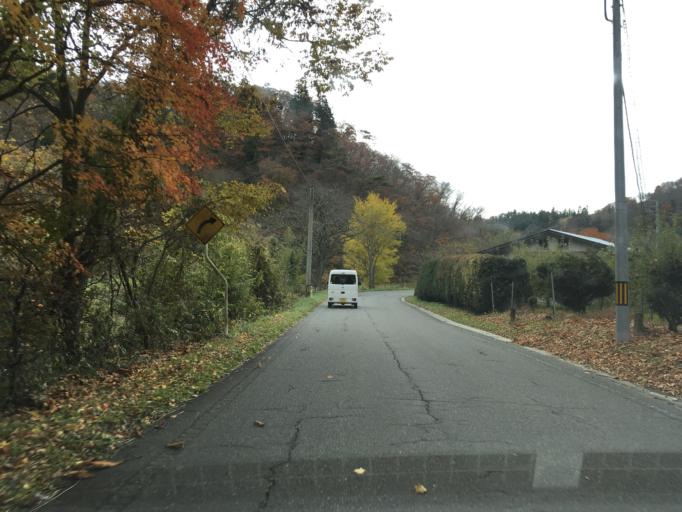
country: JP
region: Iwate
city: Mizusawa
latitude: 39.0916
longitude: 141.3471
